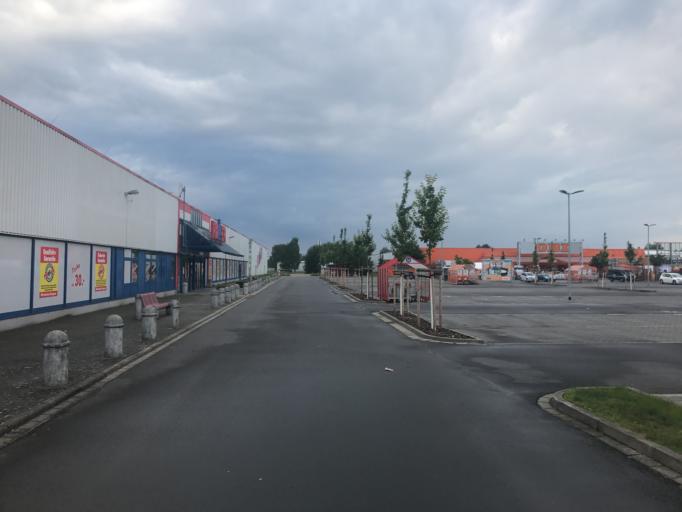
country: DE
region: Brandenburg
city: Melchow
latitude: 52.8393
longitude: 13.6983
